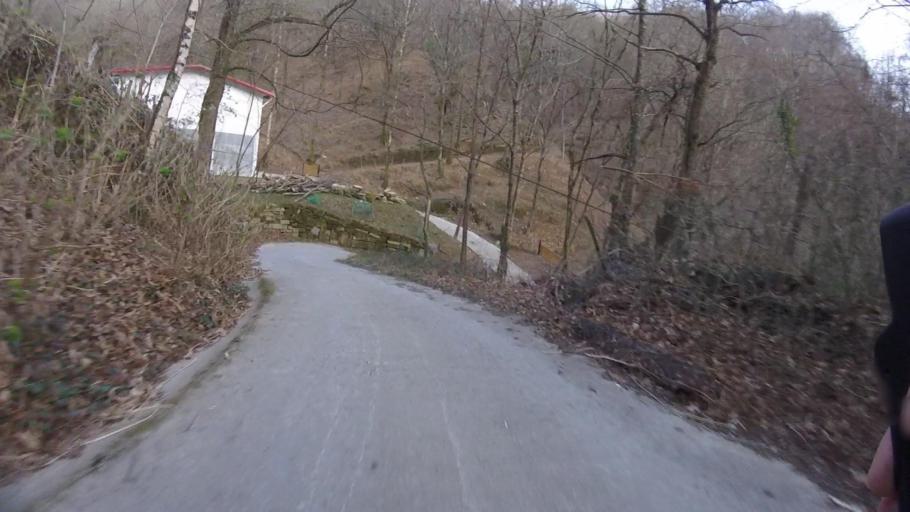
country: ES
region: Basque Country
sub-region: Provincia de Guipuzcoa
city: Errenteria
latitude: 43.2653
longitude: -1.8549
